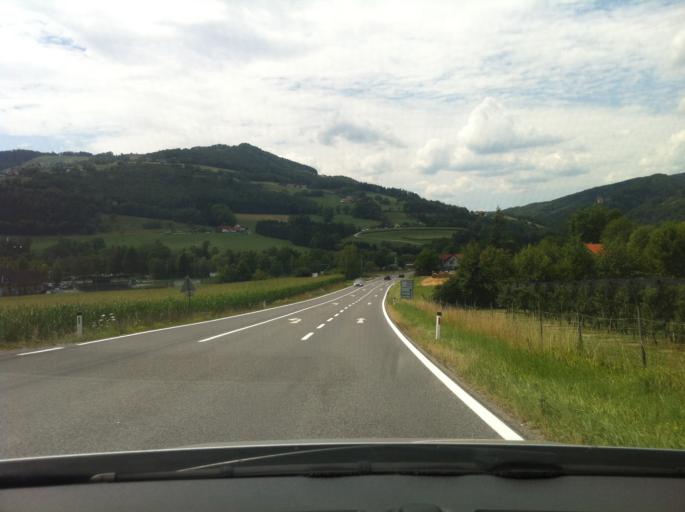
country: AT
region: Styria
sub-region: Politischer Bezirk Hartberg-Fuerstenfeld
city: Stubenberg
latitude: 47.2345
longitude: 15.8056
